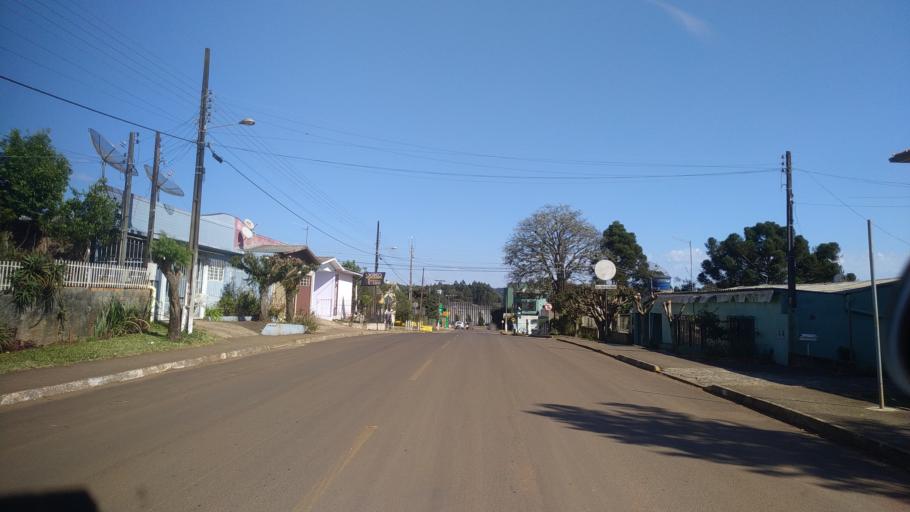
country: BR
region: Santa Catarina
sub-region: Chapeco
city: Chapeco
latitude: -27.0350
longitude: -52.6306
